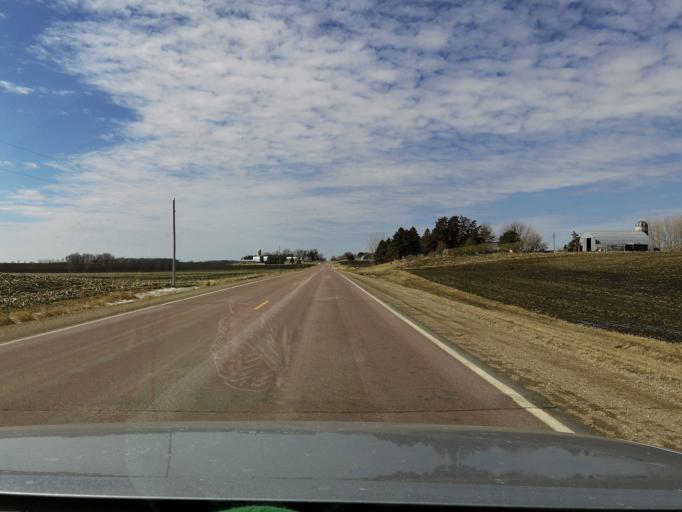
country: US
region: Minnesota
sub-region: Le Sueur County
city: Montgomery
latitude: 44.4860
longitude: -93.6423
